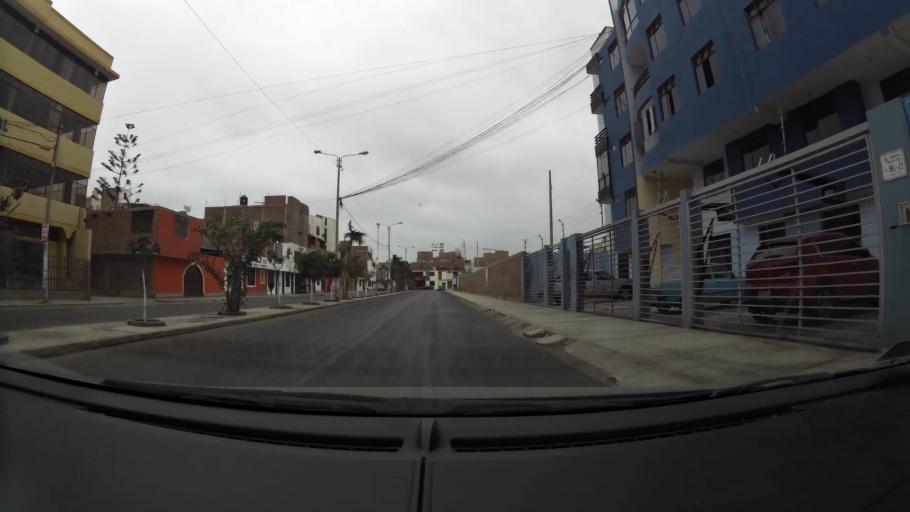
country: PE
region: La Libertad
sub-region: Provincia de Trujillo
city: Trujillo
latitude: -8.1214
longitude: -79.0283
